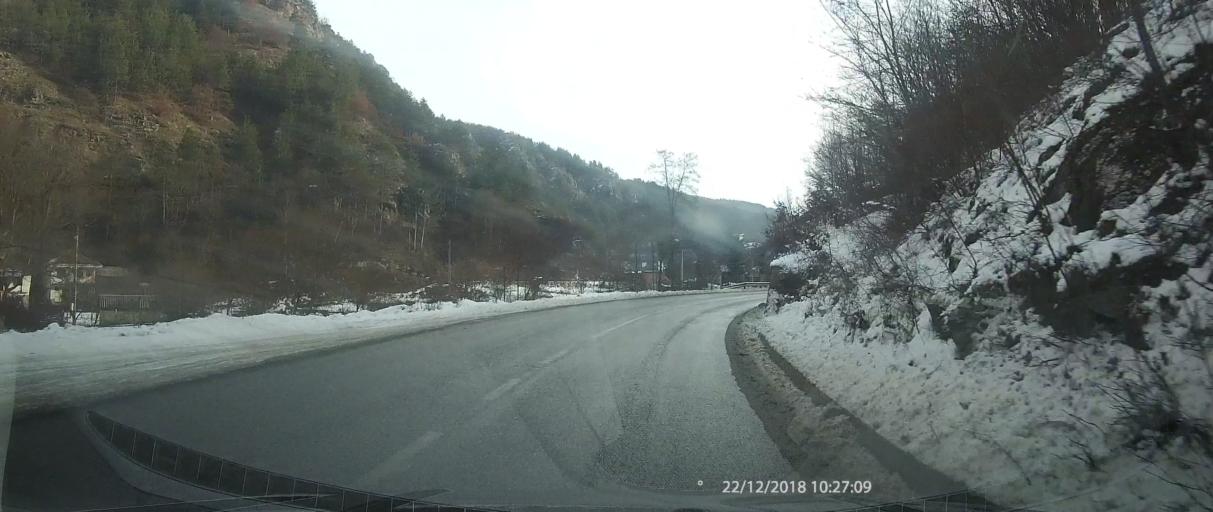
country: MK
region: Kriva Palanka
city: Kriva Palanka
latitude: 42.2307
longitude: 22.3643
